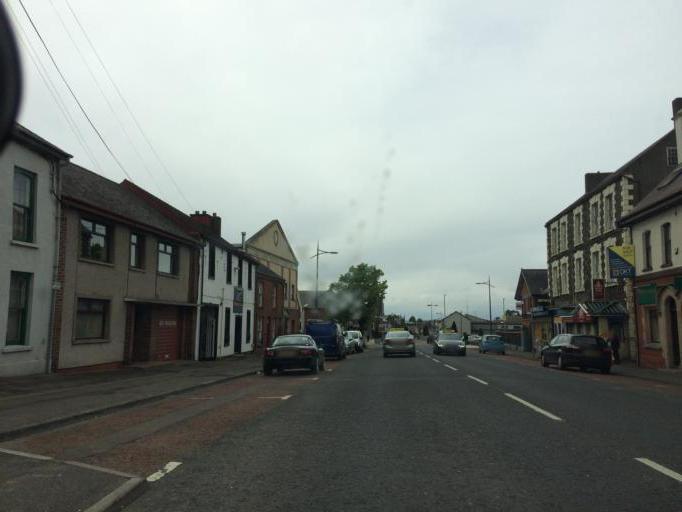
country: GB
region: Northern Ireland
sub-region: Antrim Borough
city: Antrim
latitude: 54.7135
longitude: -6.2133
